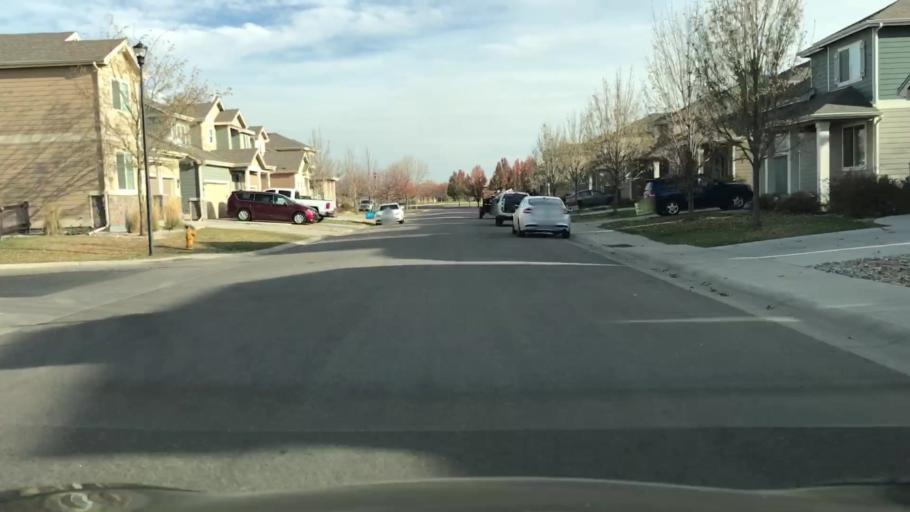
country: US
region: Colorado
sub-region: Larimer County
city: Fort Collins
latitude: 40.5914
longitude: -105.0424
